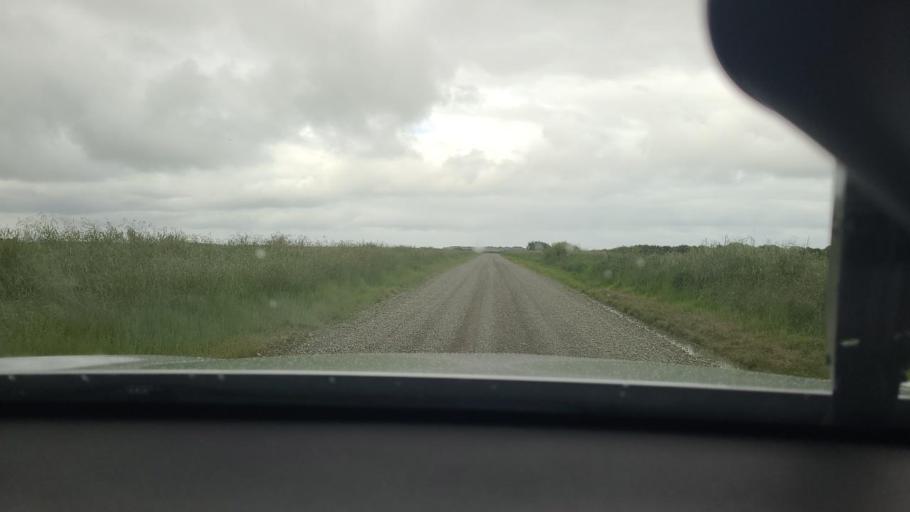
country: NZ
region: Southland
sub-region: Invercargill City
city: Invercargill
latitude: -46.3606
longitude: 168.2507
